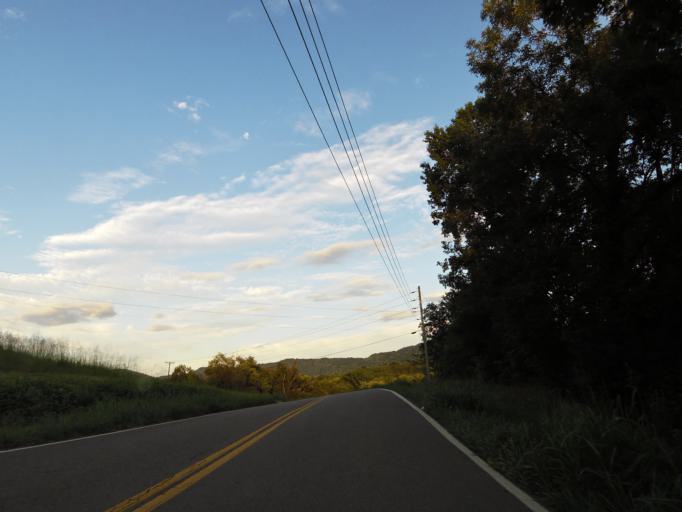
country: US
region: Tennessee
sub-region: Union County
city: Luttrell
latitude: 36.2358
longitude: -83.6998
